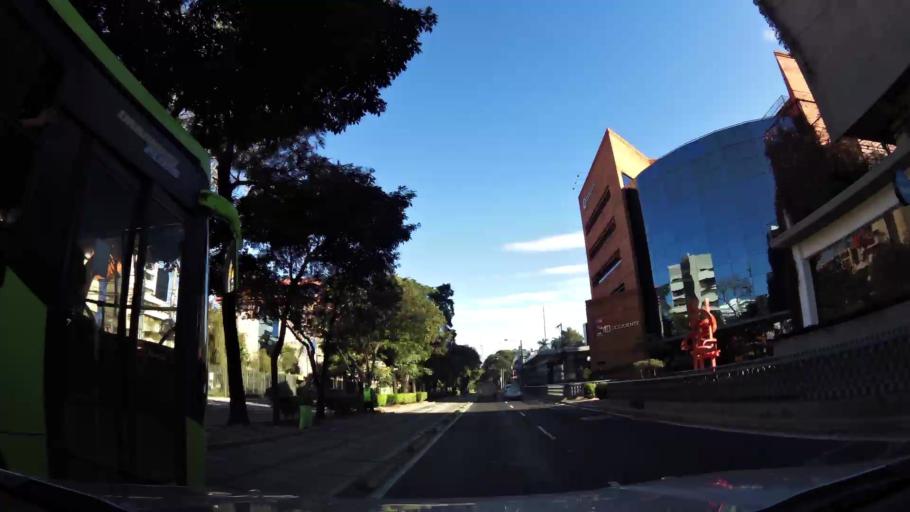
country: GT
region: Guatemala
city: Guatemala City
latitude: 14.6068
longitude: -90.5177
